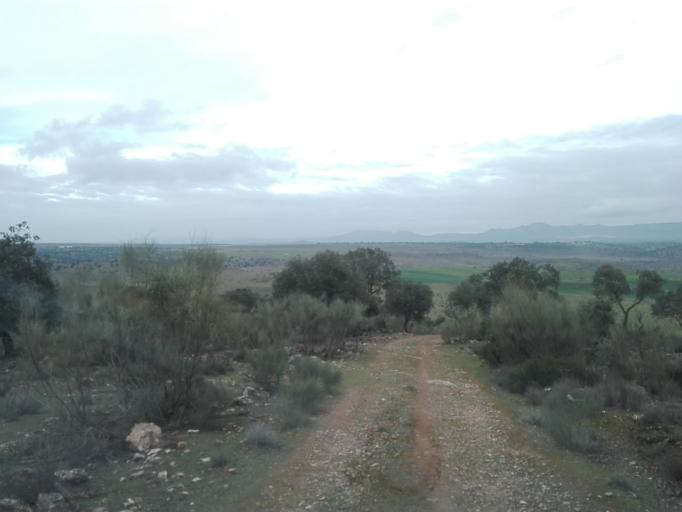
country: ES
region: Extremadura
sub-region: Provincia de Badajoz
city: Hinojosa del Valle
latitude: 38.4410
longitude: -6.1888
